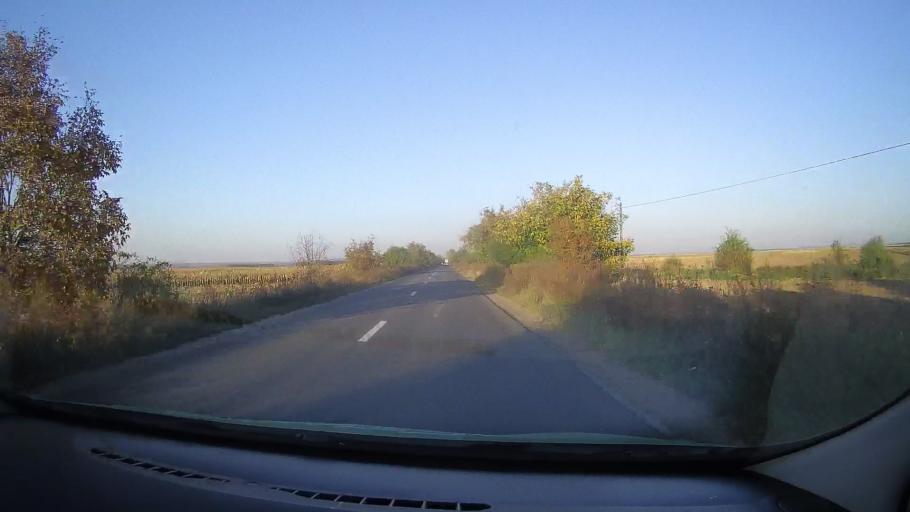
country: RO
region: Bihor
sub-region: Comuna Cetariu
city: Cetariu
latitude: 47.1898
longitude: 21.9933
